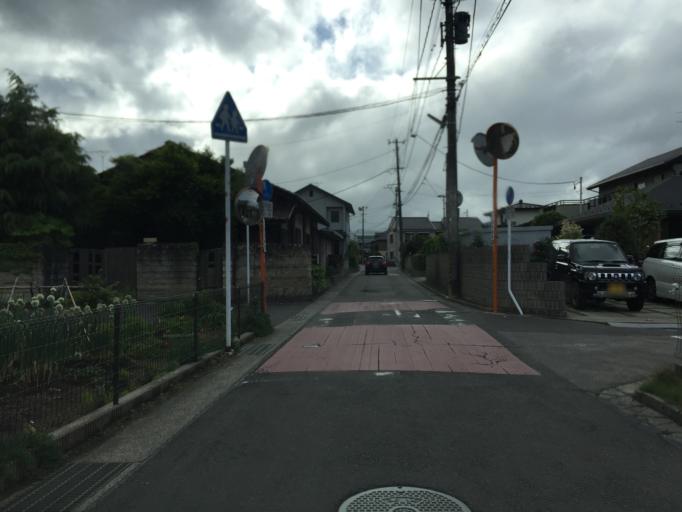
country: JP
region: Fukushima
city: Fukushima-shi
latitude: 37.7701
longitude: 140.4504
